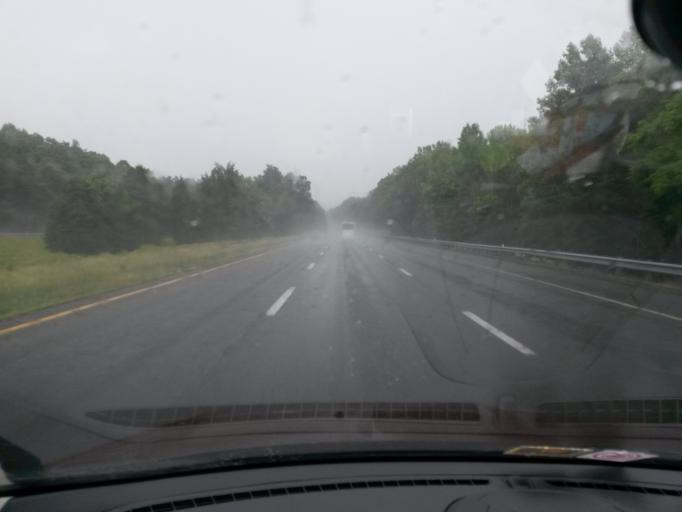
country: US
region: Virginia
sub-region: Goochland County
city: Goochland
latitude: 37.8410
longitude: -77.9788
